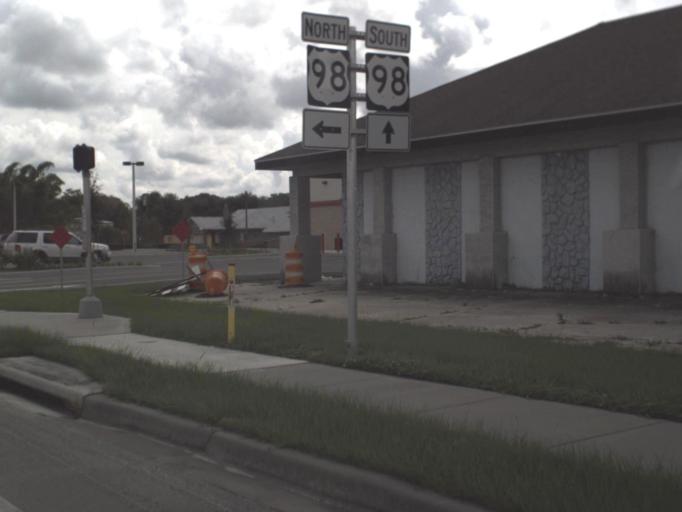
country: US
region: Florida
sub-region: Okeechobee County
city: Okeechobee
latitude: 27.2435
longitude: -80.8493
